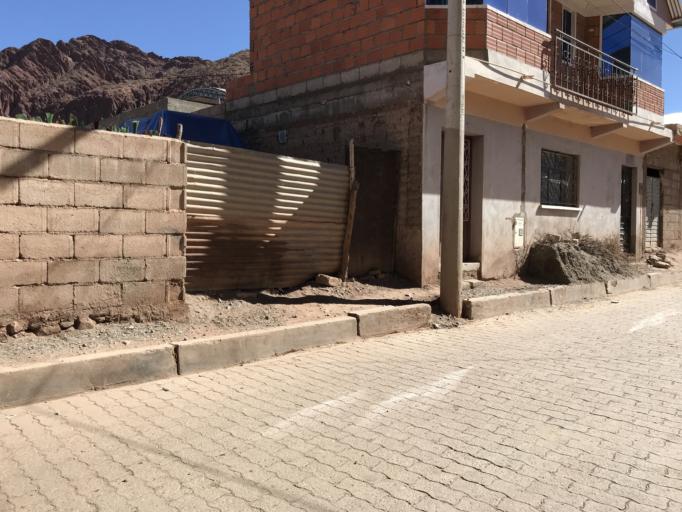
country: BO
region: Potosi
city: Tupiza
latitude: -21.4269
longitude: -65.7353
